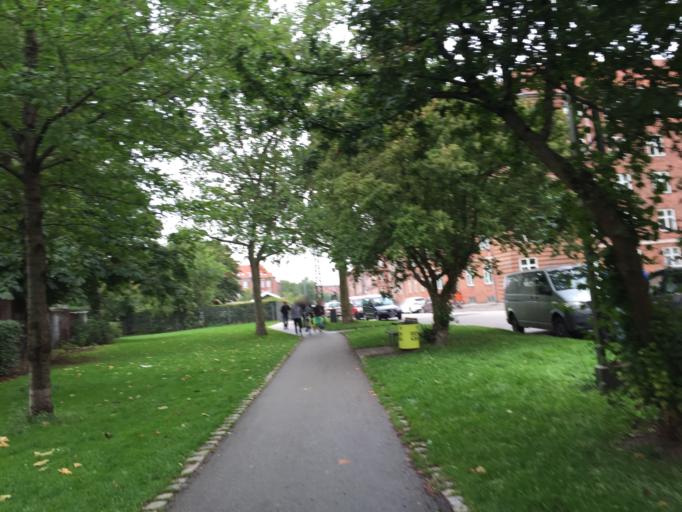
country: DK
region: Capital Region
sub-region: Kobenhavn
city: Christianshavn
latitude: 55.6630
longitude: 12.6192
